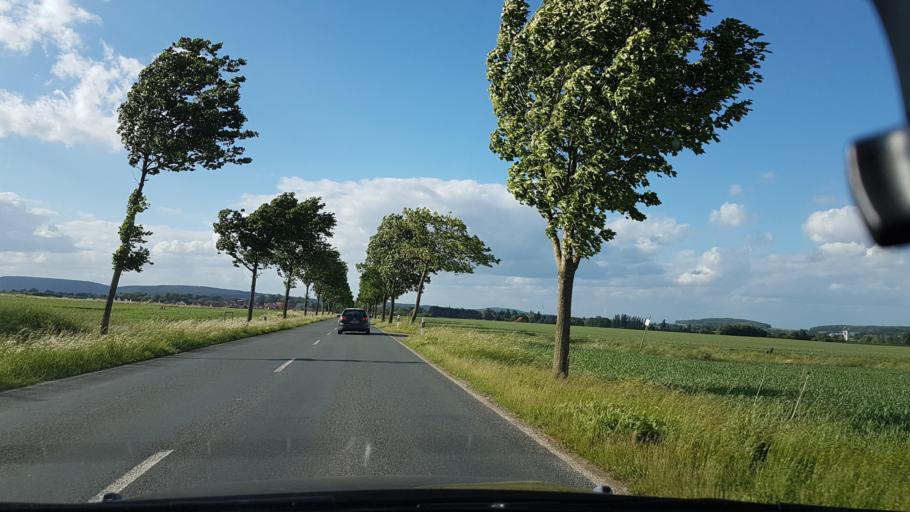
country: DE
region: Lower Saxony
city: Elze
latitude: 52.1568
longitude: 9.6627
